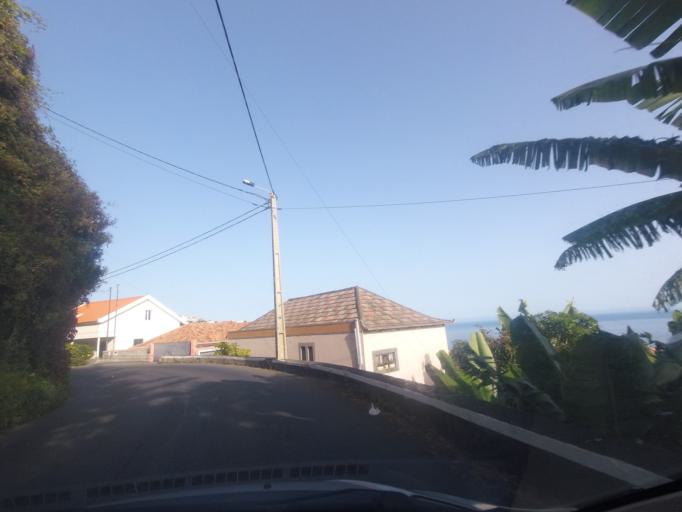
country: PT
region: Madeira
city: Ponta do Sol
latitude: 32.6846
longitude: -17.1057
